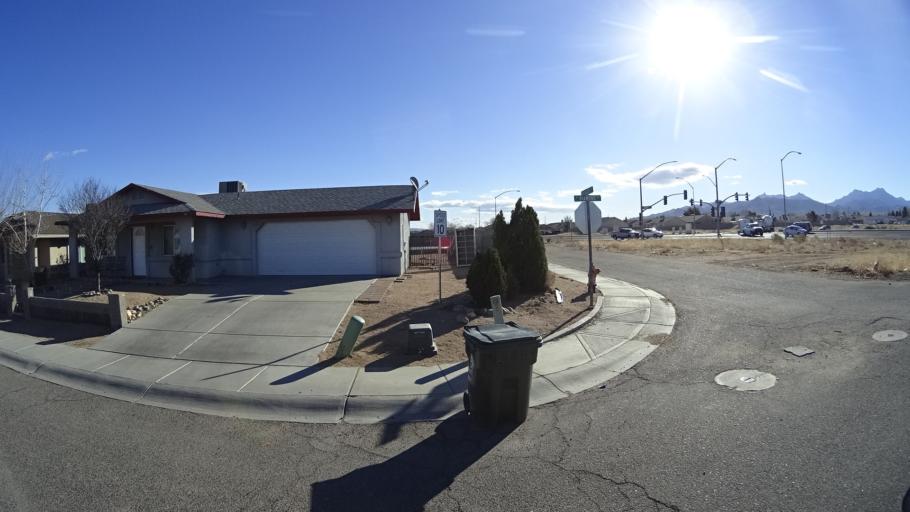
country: US
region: Arizona
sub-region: Mohave County
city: New Kingman-Butler
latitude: 35.2230
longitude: -113.9993
